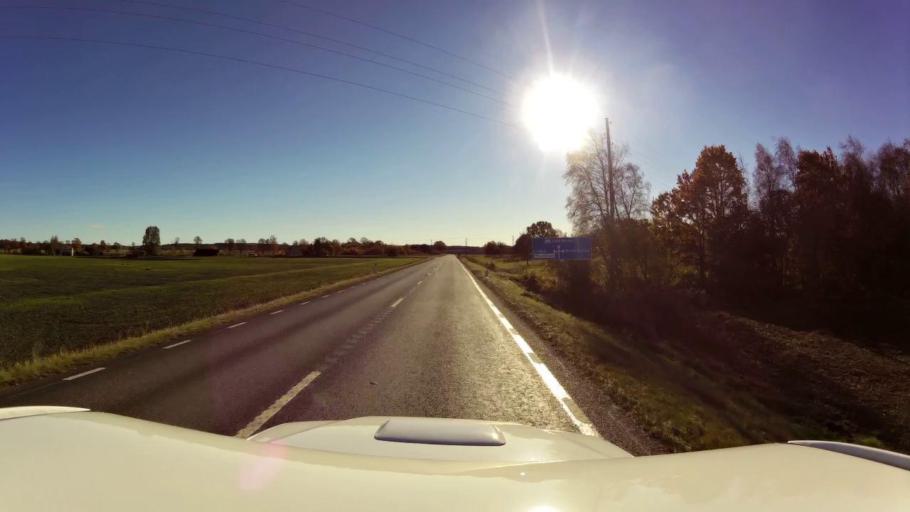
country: SE
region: OEstergoetland
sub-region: Linkopings Kommun
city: Ljungsbro
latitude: 58.5222
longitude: 15.4210
